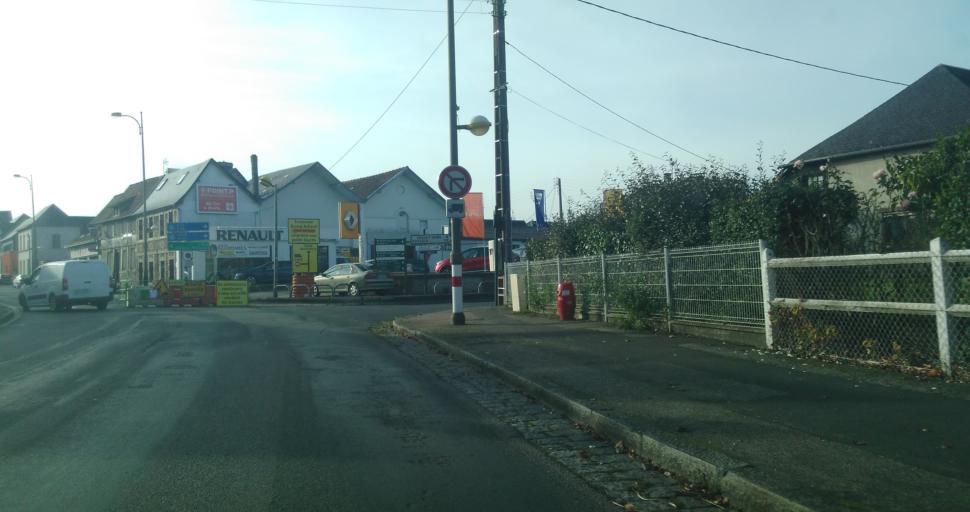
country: FR
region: Haute-Normandie
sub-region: Departement de l'Eure
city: Bourg-Achard
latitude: 49.3564
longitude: 0.8216
